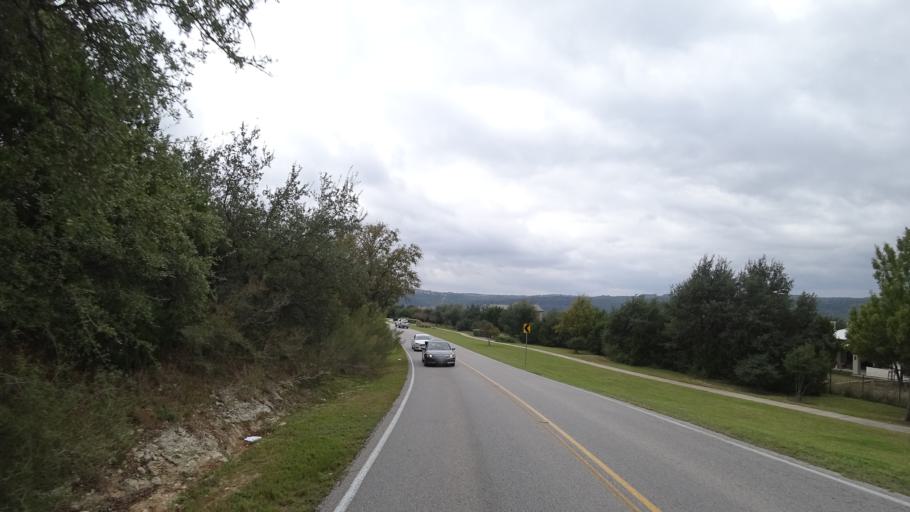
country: US
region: Texas
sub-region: Travis County
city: Bee Cave
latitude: 30.3428
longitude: -97.9213
